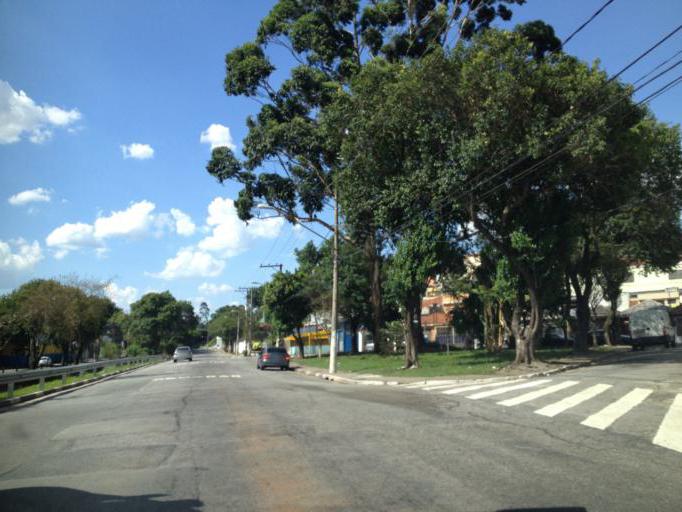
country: BR
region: Sao Paulo
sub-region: Guarulhos
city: Guarulhos
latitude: -23.5107
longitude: -46.5710
